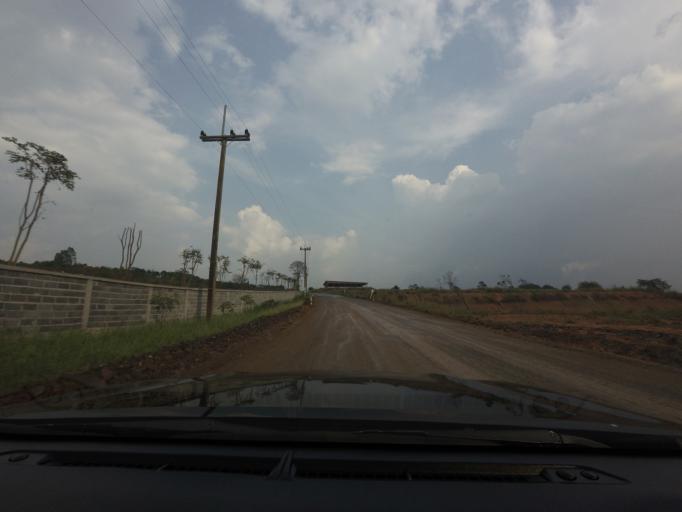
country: TH
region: Nakhon Ratchasima
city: Wang Nam Khiao
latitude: 14.4105
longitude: 101.7478
